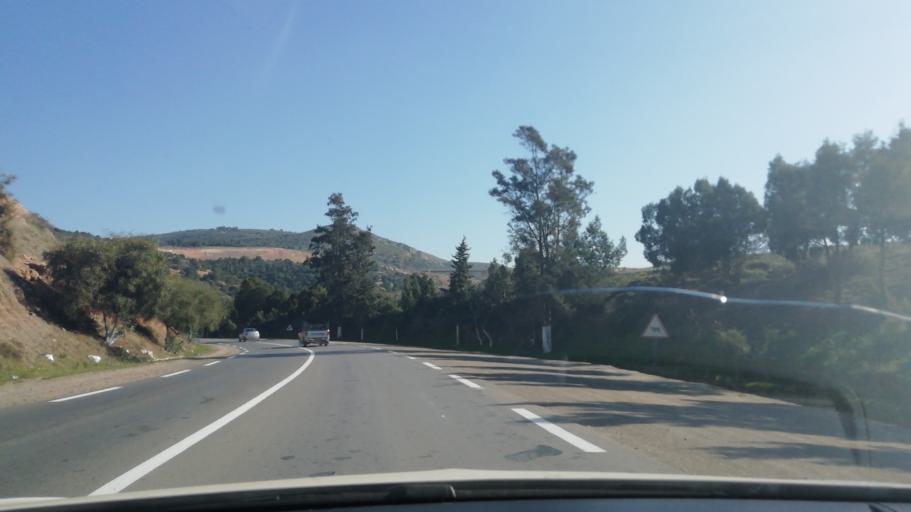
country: DZ
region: Tlemcen
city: Nedroma
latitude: 35.0929
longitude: -1.8300
